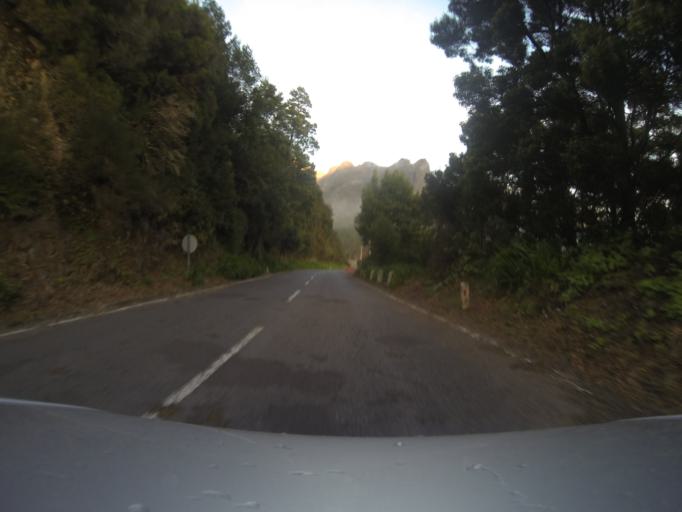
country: PT
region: Madeira
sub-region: Sao Vicente
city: Sao Vicente
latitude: 32.7545
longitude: -17.0200
